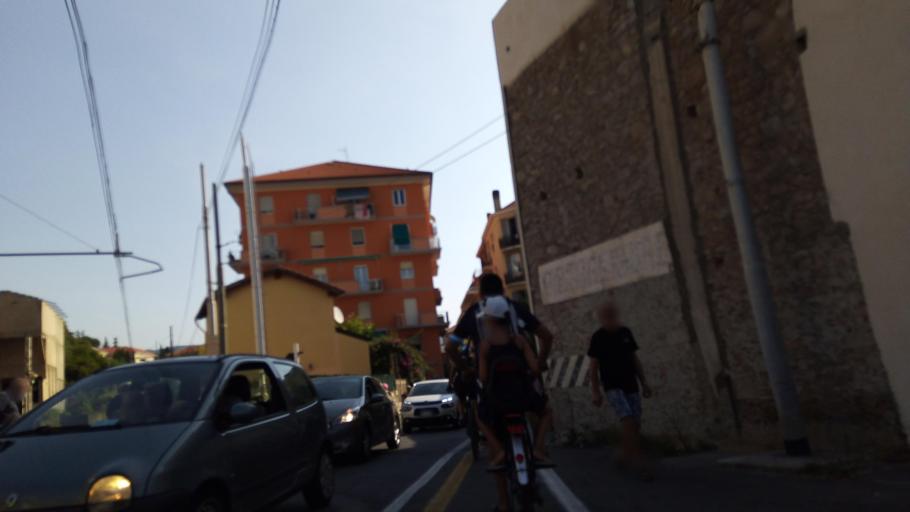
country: IT
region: Liguria
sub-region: Provincia di Savona
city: Pietra Ligure
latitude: 44.1477
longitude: 8.2801
